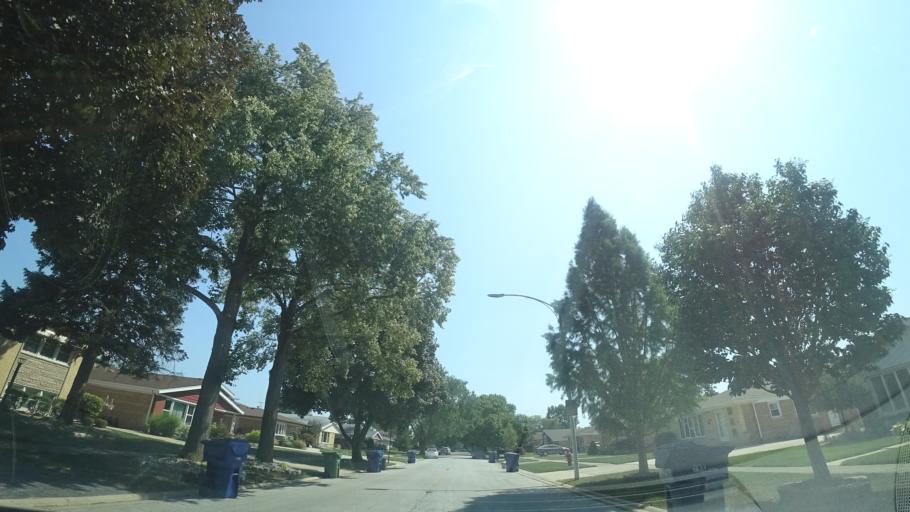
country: US
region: Illinois
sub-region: Cook County
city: Oak Lawn
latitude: 41.6975
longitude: -87.7448
